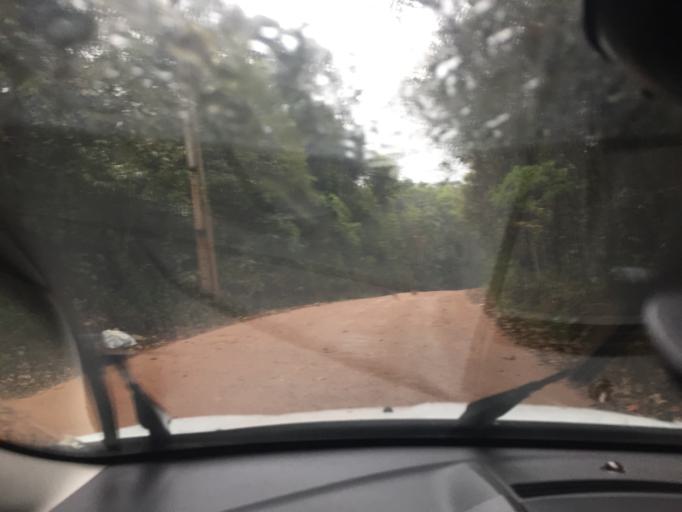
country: BR
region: Sao Paulo
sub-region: Jarinu
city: Jarinu
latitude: -23.1422
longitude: -46.7419
